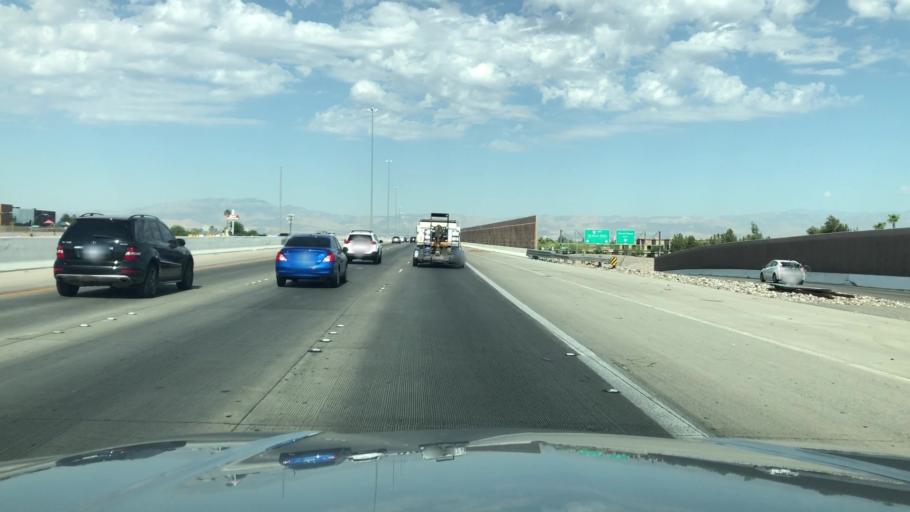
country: US
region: Nevada
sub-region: Clark County
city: Whitney
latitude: 36.0236
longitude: -115.0971
